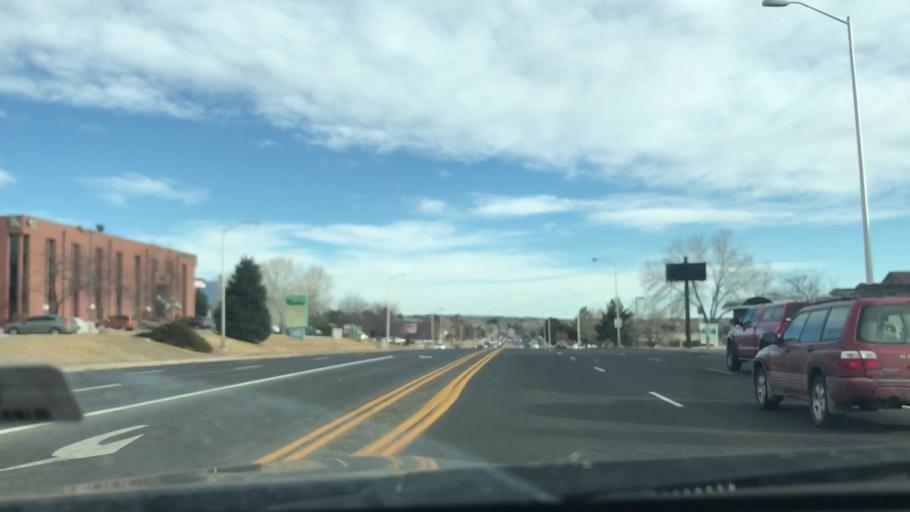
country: US
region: Colorado
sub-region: El Paso County
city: Colorado Springs
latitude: 38.9068
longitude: -104.7813
